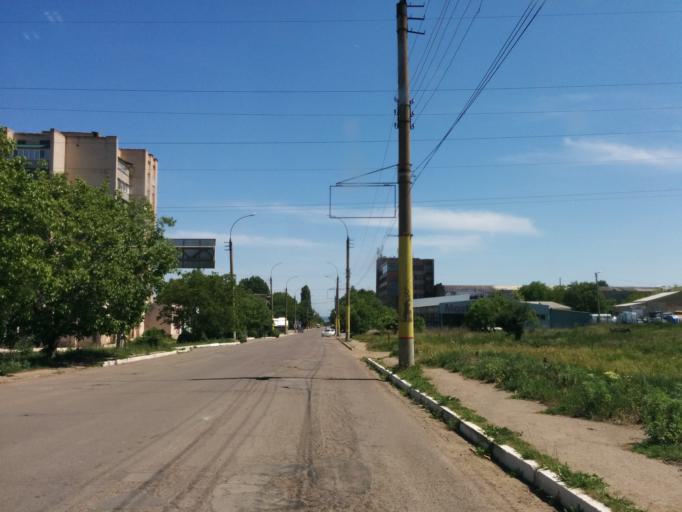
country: MD
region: Raionul Soroca
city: Soroca
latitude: 48.1628
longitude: 28.2663
